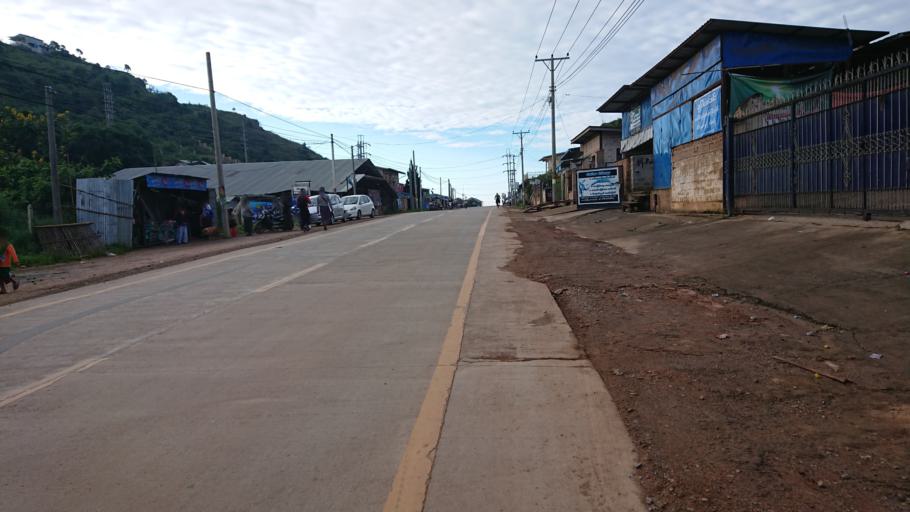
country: MM
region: Shan
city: Taunggyi
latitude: 20.7461
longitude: 97.0504
